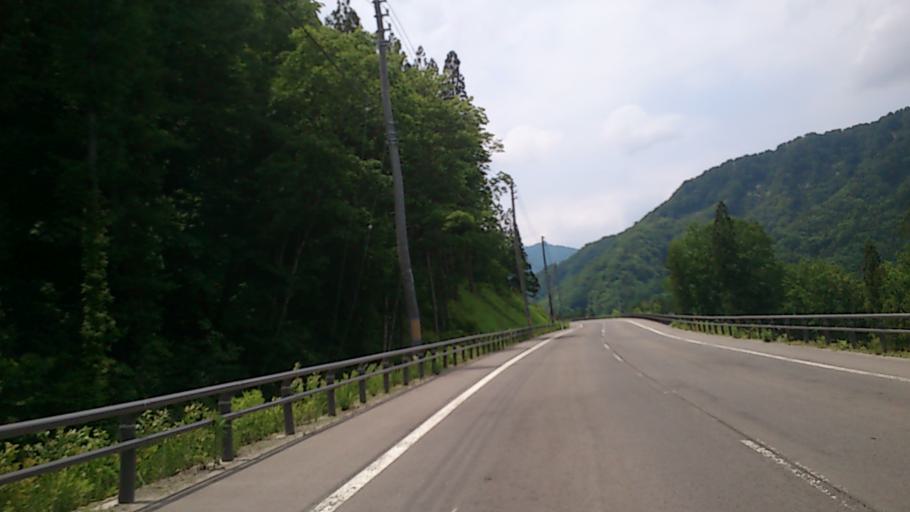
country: JP
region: Aomori
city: Hirosaki
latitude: 40.5192
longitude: 140.2098
